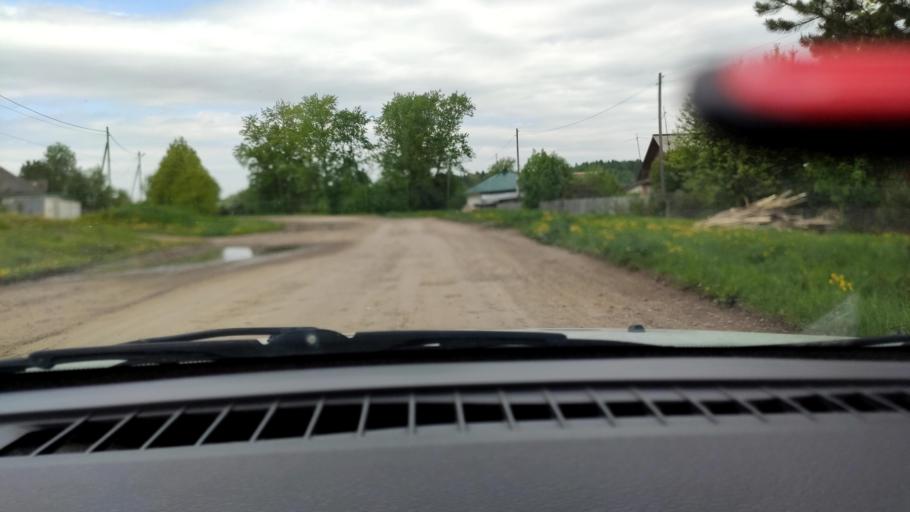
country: RU
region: Perm
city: Bershet'
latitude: 57.7306
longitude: 56.3786
